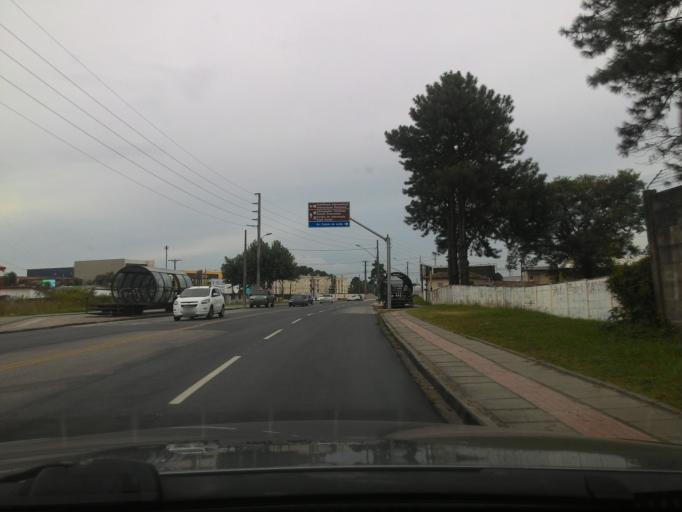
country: BR
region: Parana
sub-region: Pinhais
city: Pinhais
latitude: -25.4461
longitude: -49.1887
